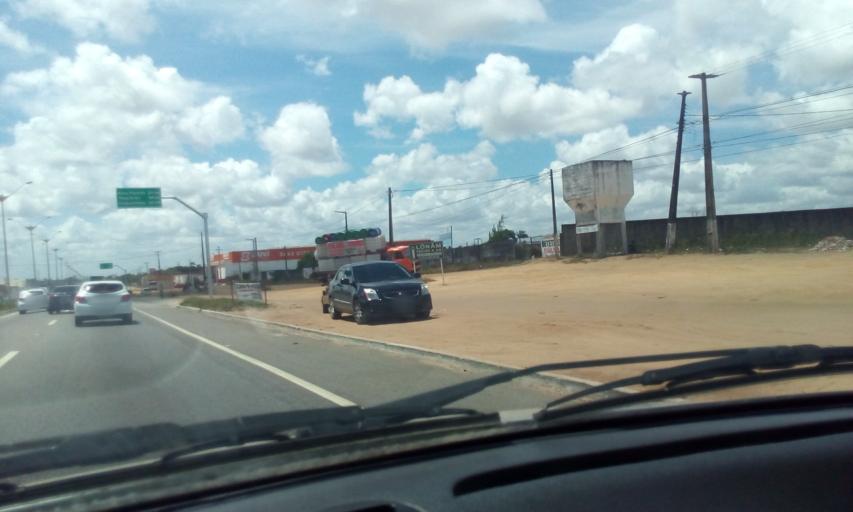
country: BR
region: Rio Grande do Norte
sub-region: Parnamirim
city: Parnamirim
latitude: -5.8962
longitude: -35.2582
